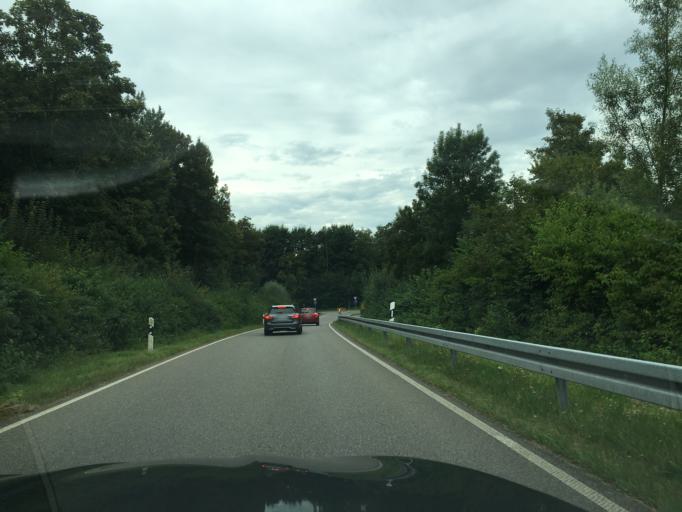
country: DE
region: Baden-Wuerttemberg
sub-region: Tuebingen Region
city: Riedlingen
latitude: 48.1536
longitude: 9.4908
